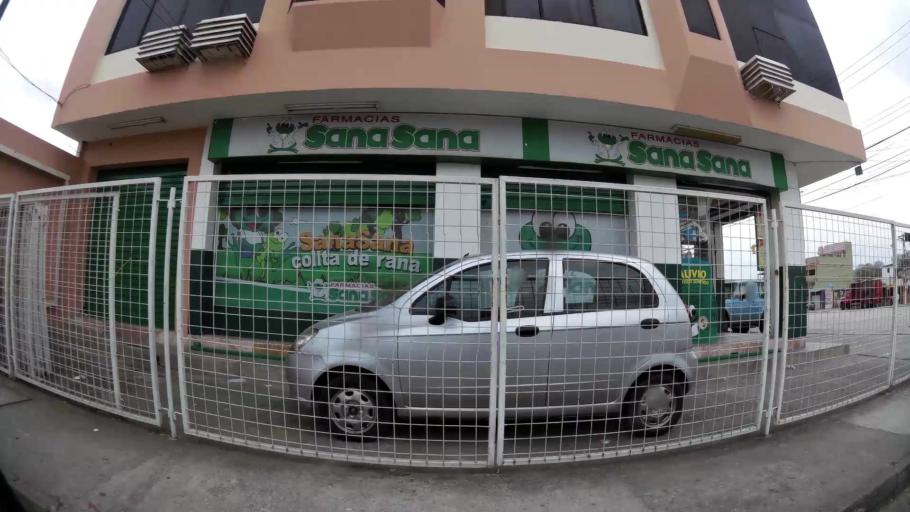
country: EC
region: Guayas
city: Eloy Alfaro
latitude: -2.1138
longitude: -79.8987
